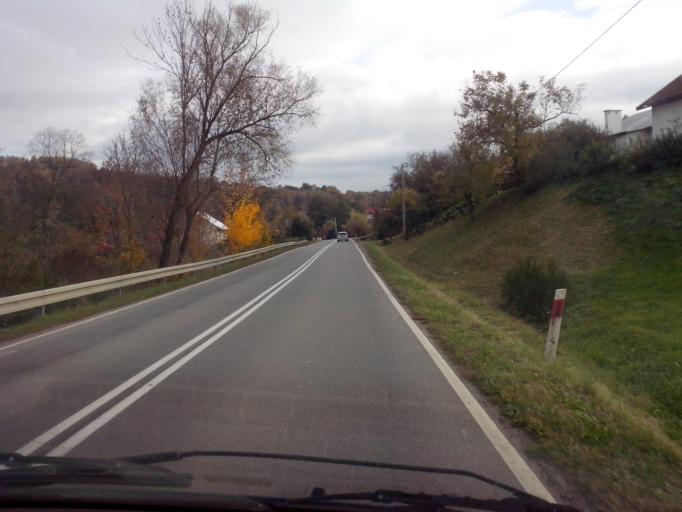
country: PL
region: Subcarpathian Voivodeship
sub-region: Powiat strzyzowski
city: Wisniowa
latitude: 49.8883
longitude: 21.6445
